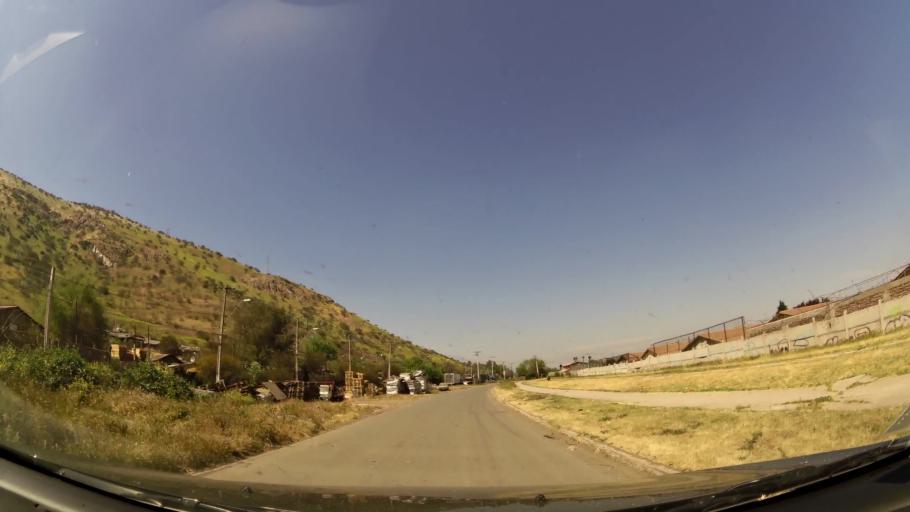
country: CL
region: Santiago Metropolitan
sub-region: Provincia de Santiago
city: Lo Prado
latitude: -33.3951
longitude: -70.7434
